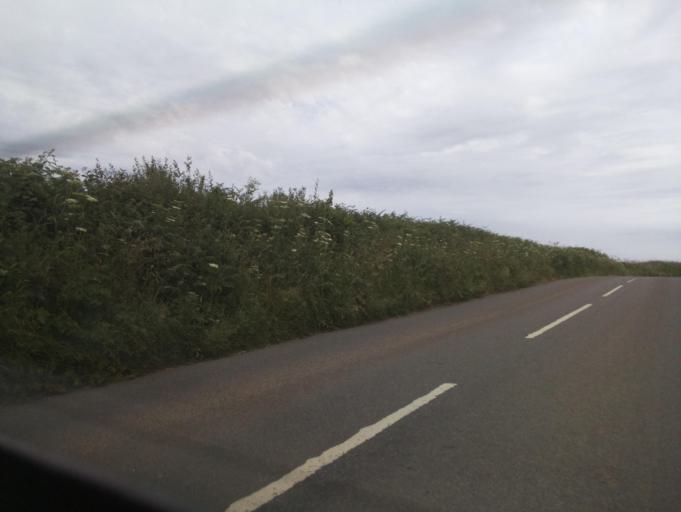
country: GB
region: England
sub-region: Devon
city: Dartmouth
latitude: 50.3626
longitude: -3.6336
